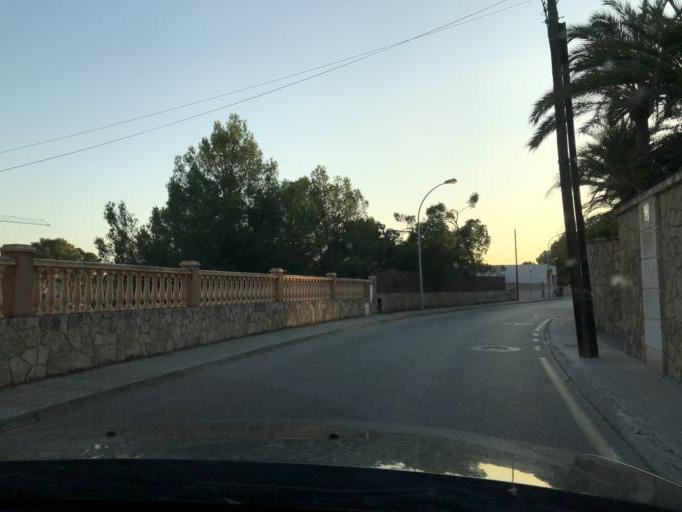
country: ES
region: Balearic Islands
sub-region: Illes Balears
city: Santa Ponsa
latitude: 39.5271
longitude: 2.4660
